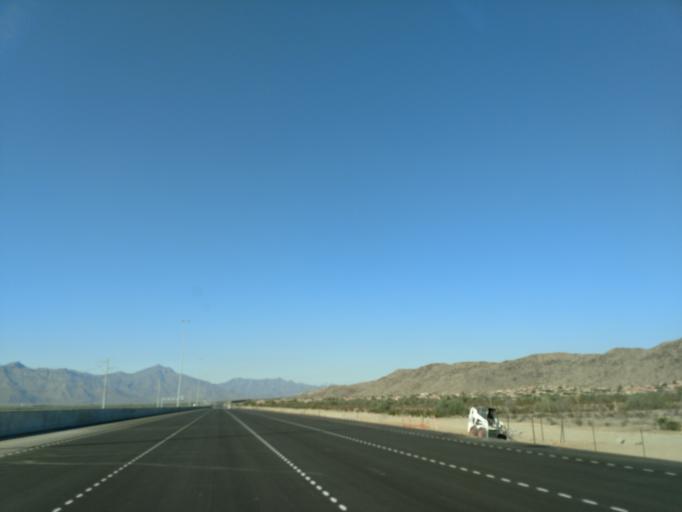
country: US
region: Arizona
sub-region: Maricopa County
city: Laveen
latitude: 33.2919
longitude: -112.1072
